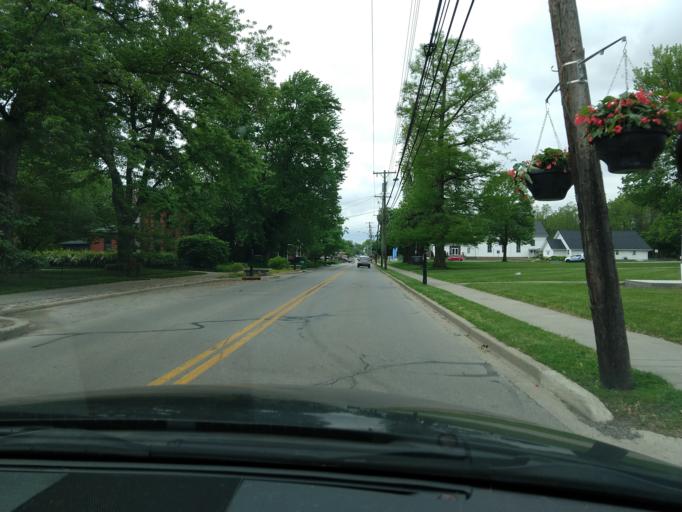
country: US
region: Indiana
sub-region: Hamilton County
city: Westfield
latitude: 40.0383
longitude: -86.1277
